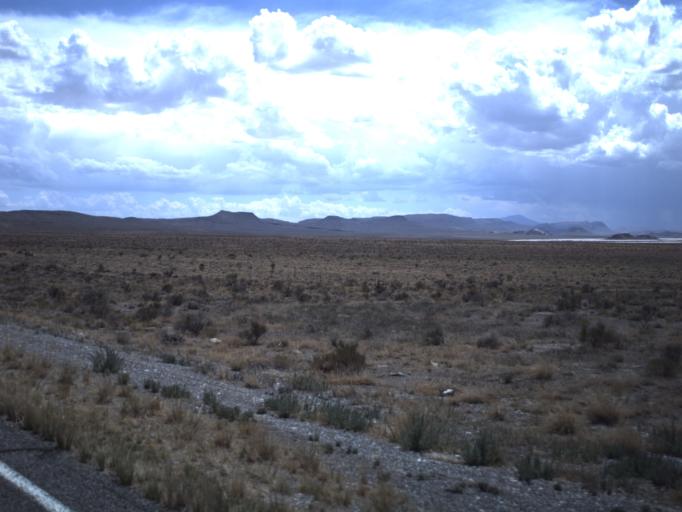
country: US
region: Utah
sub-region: Beaver County
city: Milford
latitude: 39.0269
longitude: -113.3750
